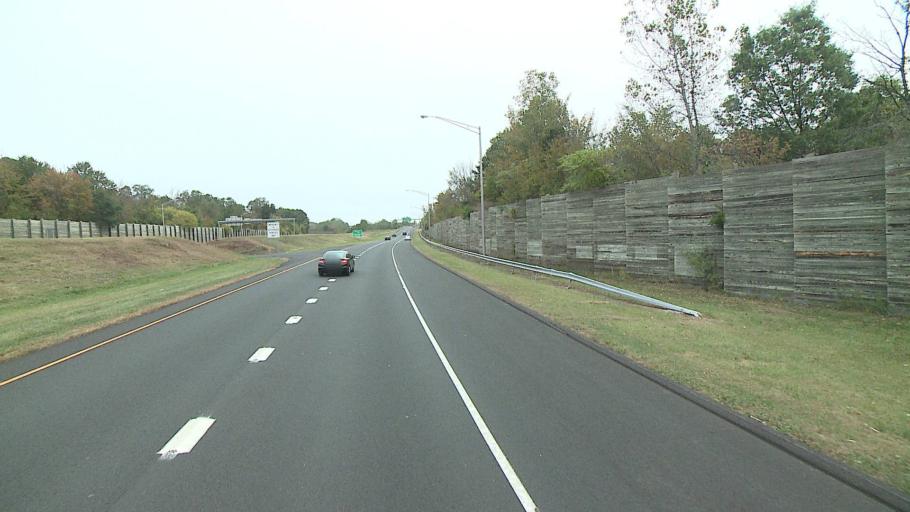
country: US
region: Connecticut
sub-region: Hartford County
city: Newington
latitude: 41.7191
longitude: -72.7704
